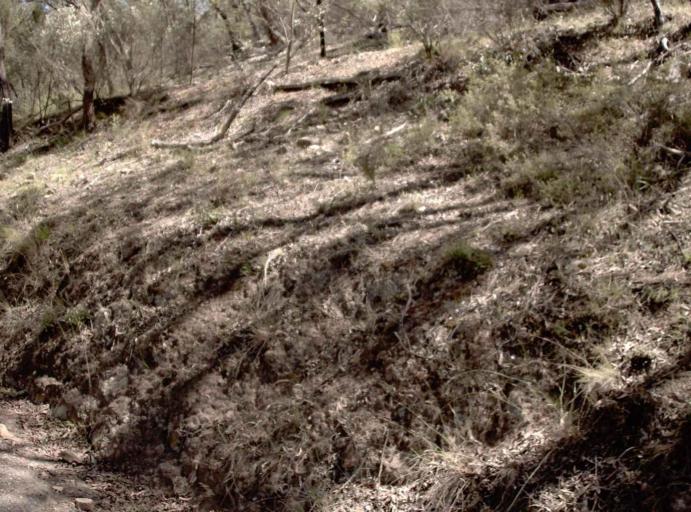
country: AU
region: New South Wales
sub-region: Bombala
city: Bombala
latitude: -37.1058
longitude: 148.6409
